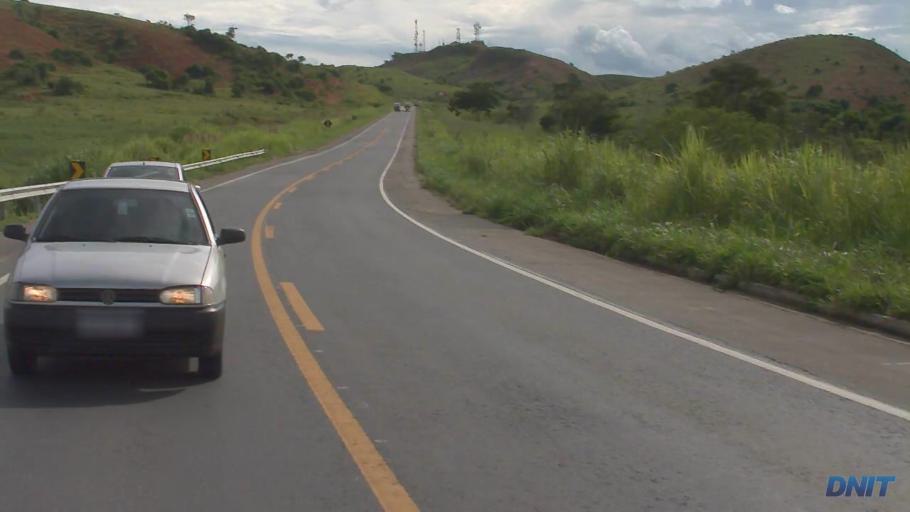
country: BR
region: Minas Gerais
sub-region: Belo Oriente
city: Belo Oriente
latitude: -19.2220
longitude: -42.3153
